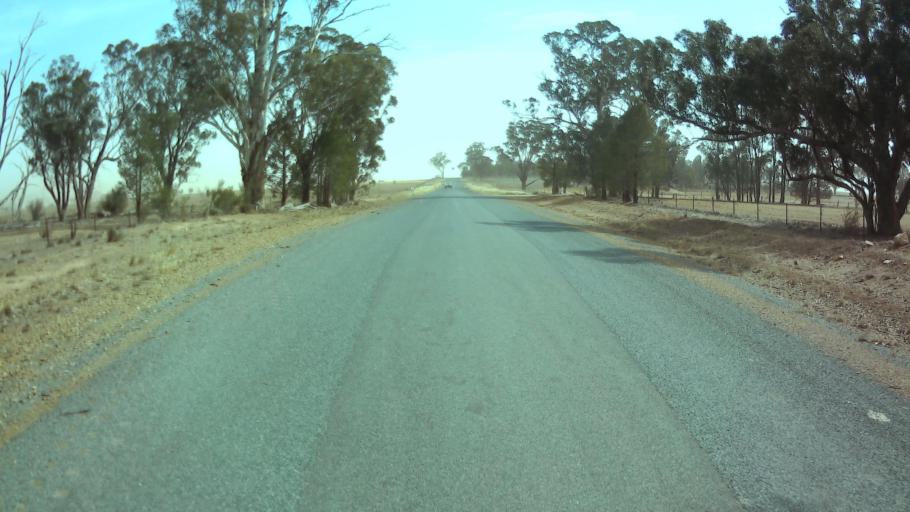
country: AU
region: New South Wales
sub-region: Weddin
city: Grenfell
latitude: -33.7513
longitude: 147.9907
